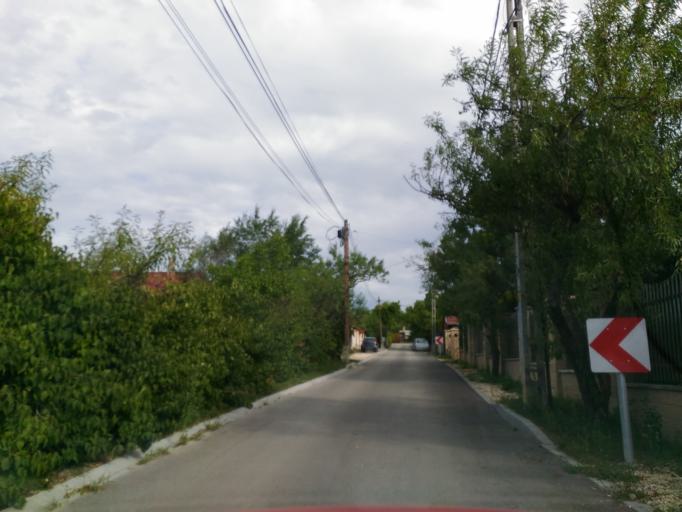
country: HU
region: Pest
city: Diosd
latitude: 47.4067
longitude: 18.9861
